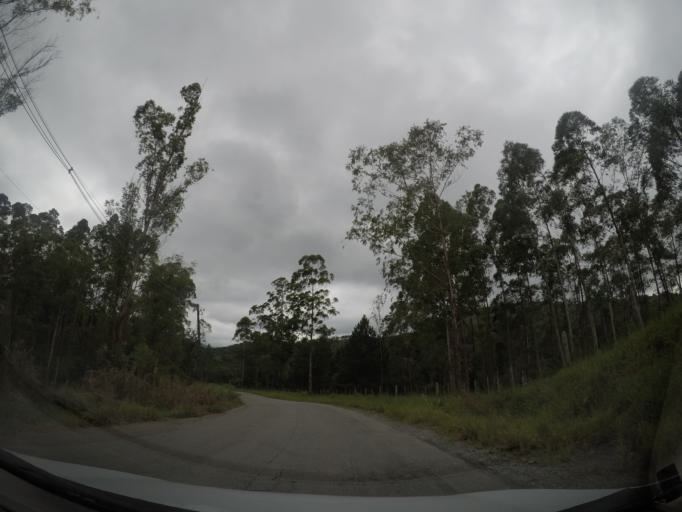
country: BR
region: Sao Paulo
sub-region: Aruja
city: Aruja
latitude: -23.3542
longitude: -46.4079
